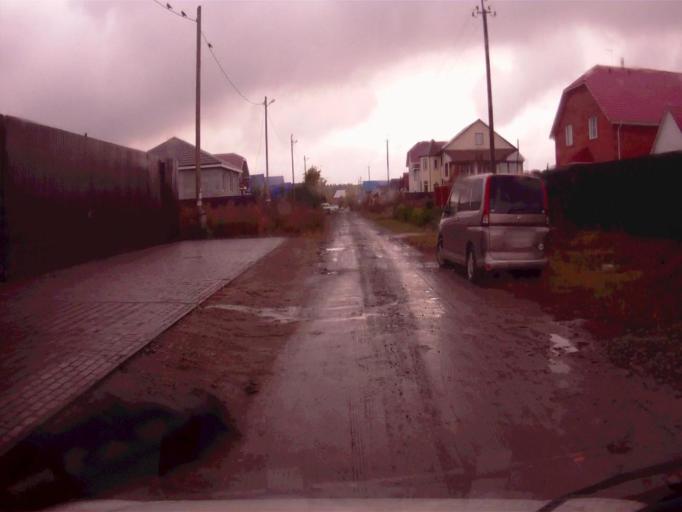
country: RU
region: Chelyabinsk
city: Dolgoderevenskoye
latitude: 55.3075
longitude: 61.3414
